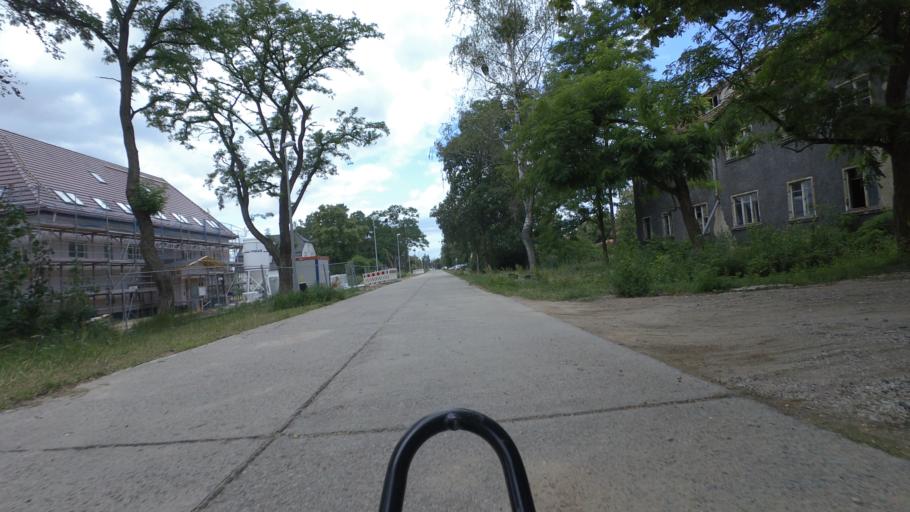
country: DE
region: Brandenburg
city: Trebbin
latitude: 52.2404
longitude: 13.1551
